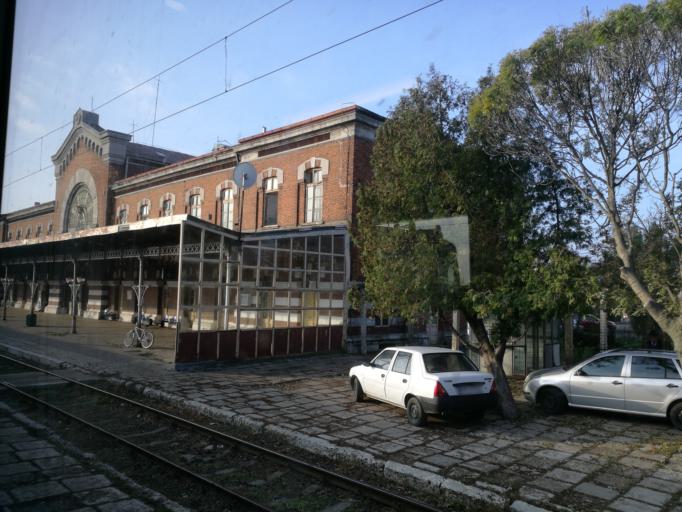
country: RO
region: Buzau
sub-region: Municipiul Ramnicu Sarat
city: Ramnicu Sarat
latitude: 45.3799
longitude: 27.0581
